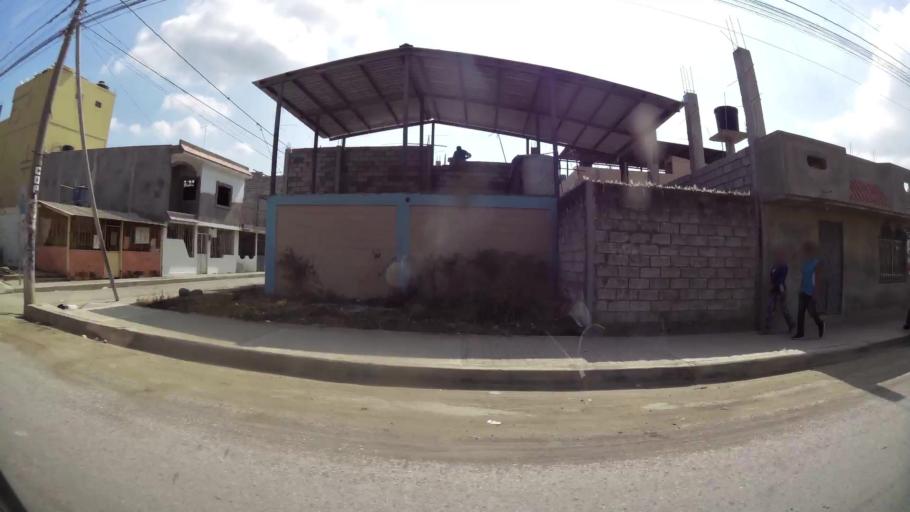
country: EC
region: Guayas
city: Eloy Alfaro
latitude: -2.1682
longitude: -79.8300
